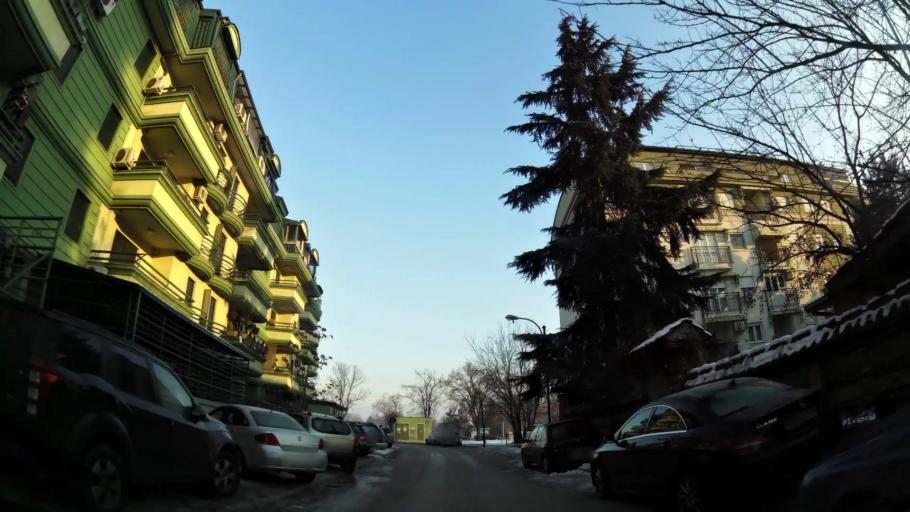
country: MK
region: Karpos
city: Skopje
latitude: 42.0060
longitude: 21.4104
